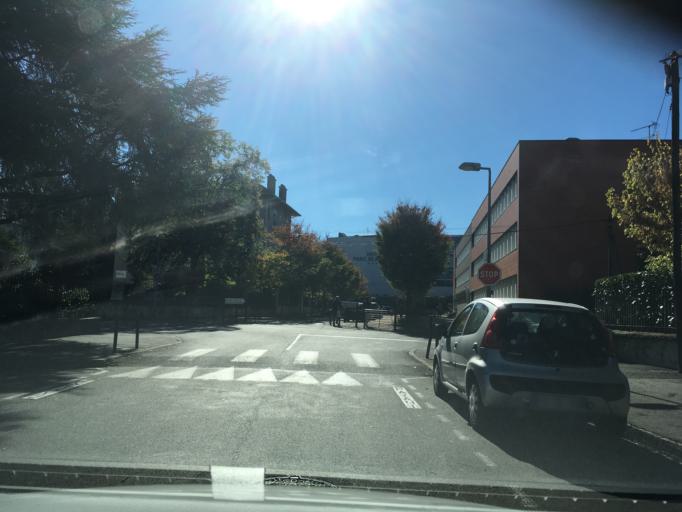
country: FR
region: Aquitaine
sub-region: Departement des Pyrenees-Atlantiques
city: Pau
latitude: 43.2986
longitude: -0.3597
